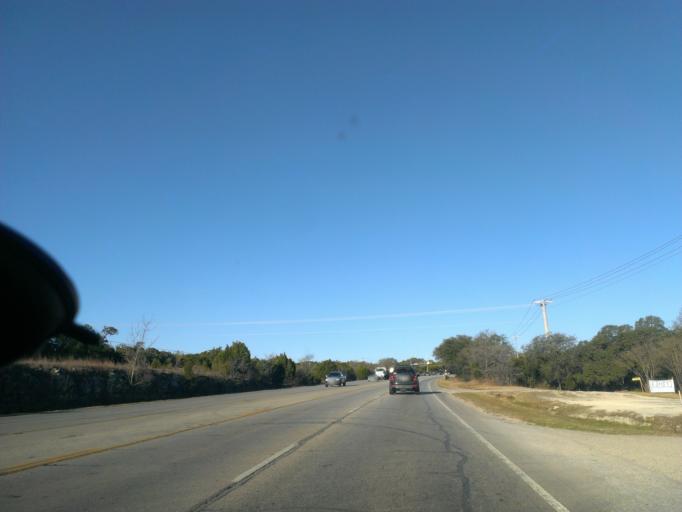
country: US
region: Texas
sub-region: Travis County
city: Barton Creek
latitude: 30.2297
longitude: -97.8923
